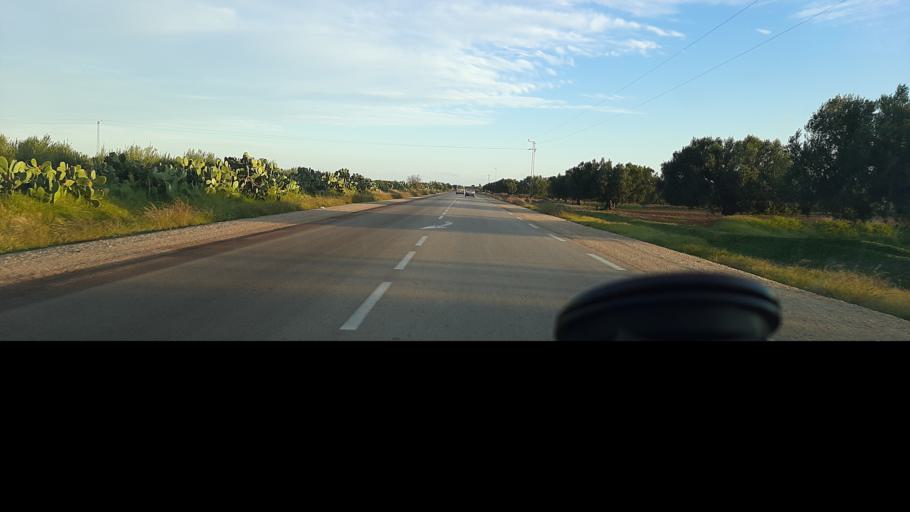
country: TN
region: Safaqis
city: Sfax
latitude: 34.9322
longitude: 10.6198
